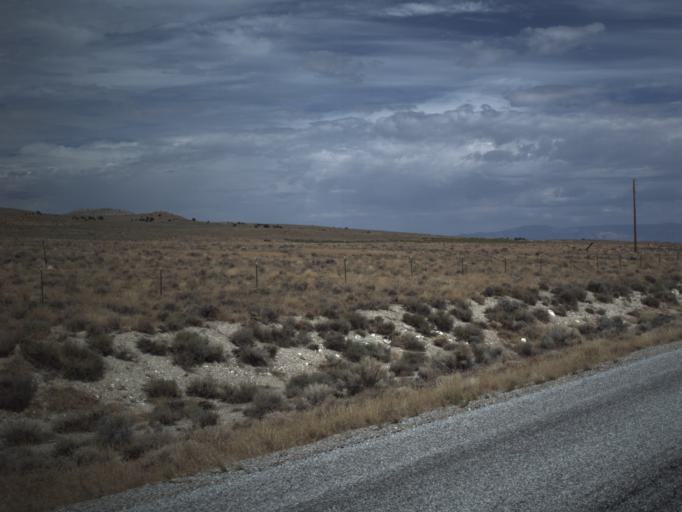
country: US
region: Utah
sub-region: Tooele County
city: Wendover
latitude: 41.4957
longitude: -113.6132
